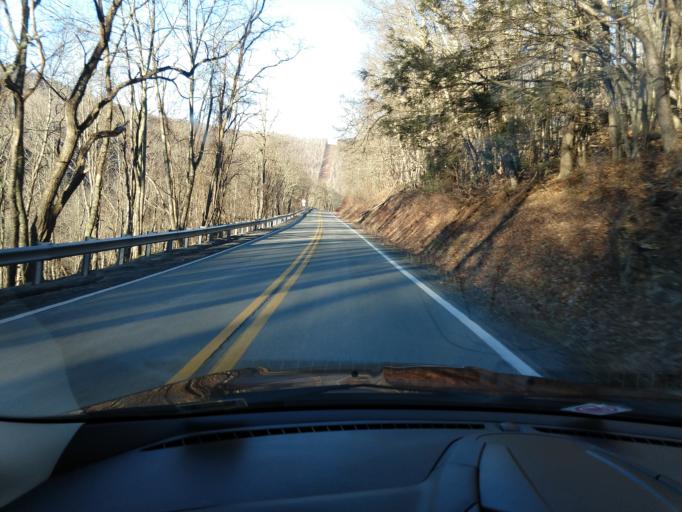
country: US
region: Virginia
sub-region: Highland County
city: Monterey
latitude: 38.4938
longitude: -79.7035
